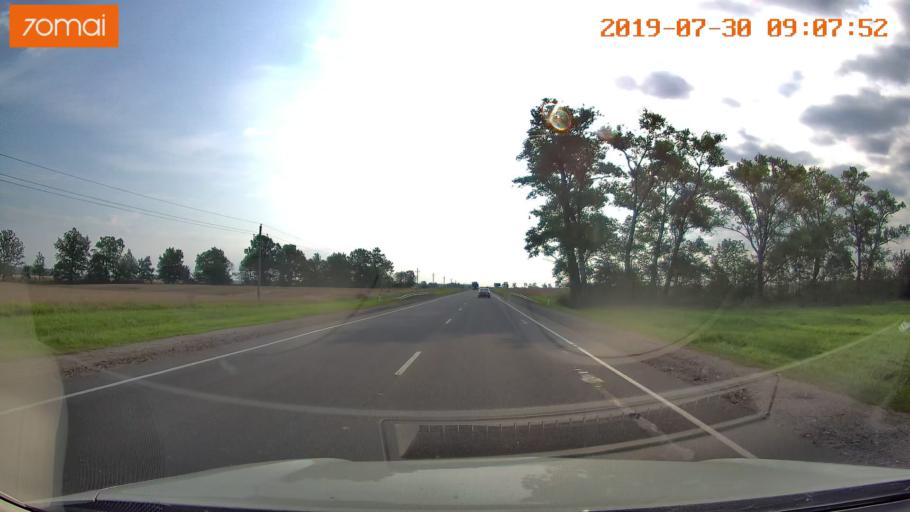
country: RU
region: Kaliningrad
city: Gusev
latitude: 54.6119
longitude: 22.3728
